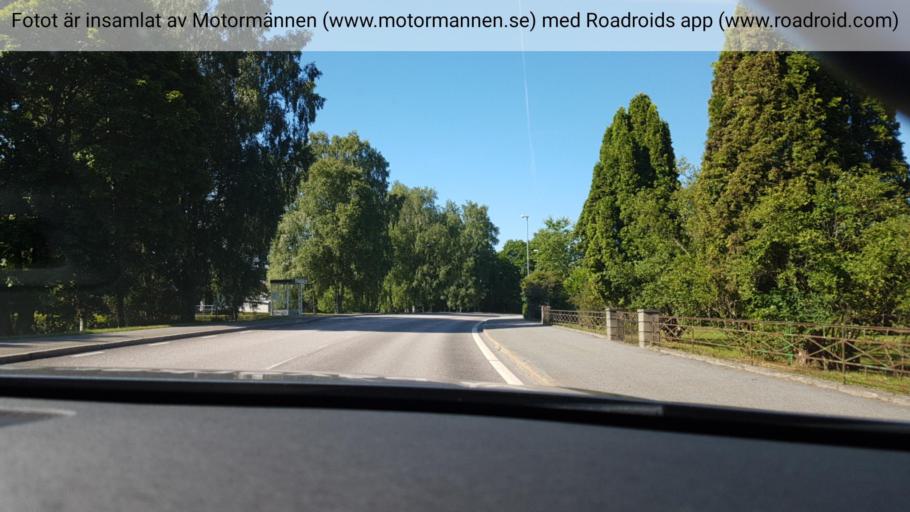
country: SE
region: Vaestra Goetaland
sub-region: Ulricehamns Kommun
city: Ulricehamn
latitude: 57.9347
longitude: 13.5007
